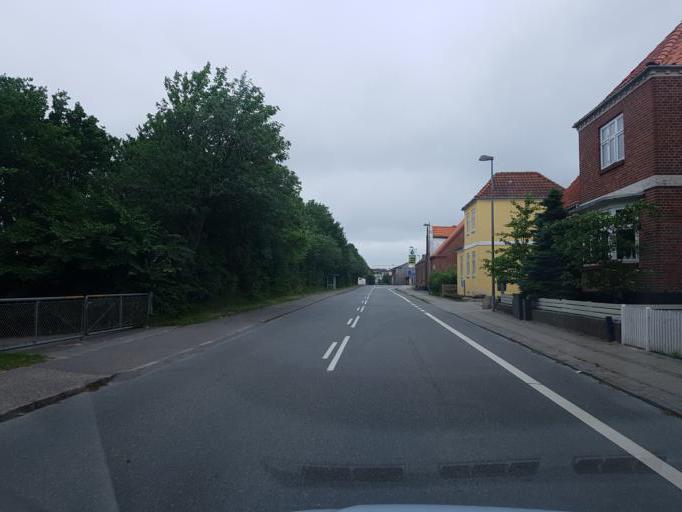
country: DK
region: South Denmark
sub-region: Varde Kommune
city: Varde
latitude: 55.6150
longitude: 8.4836
